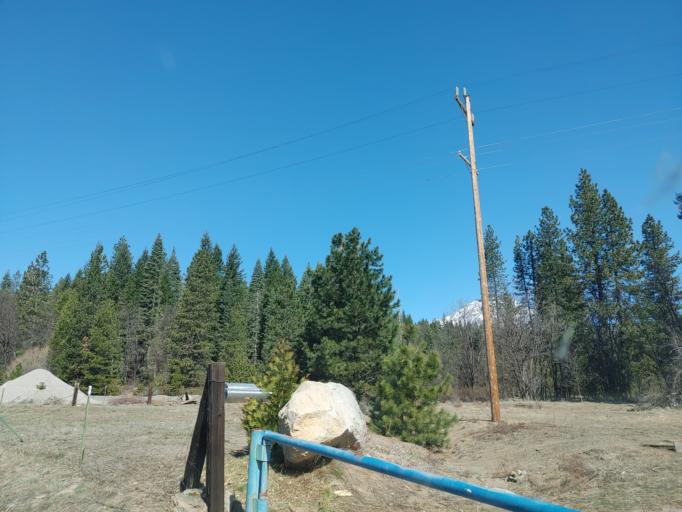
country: US
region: California
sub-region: Siskiyou County
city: McCloud
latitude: 41.2626
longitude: -122.1388
